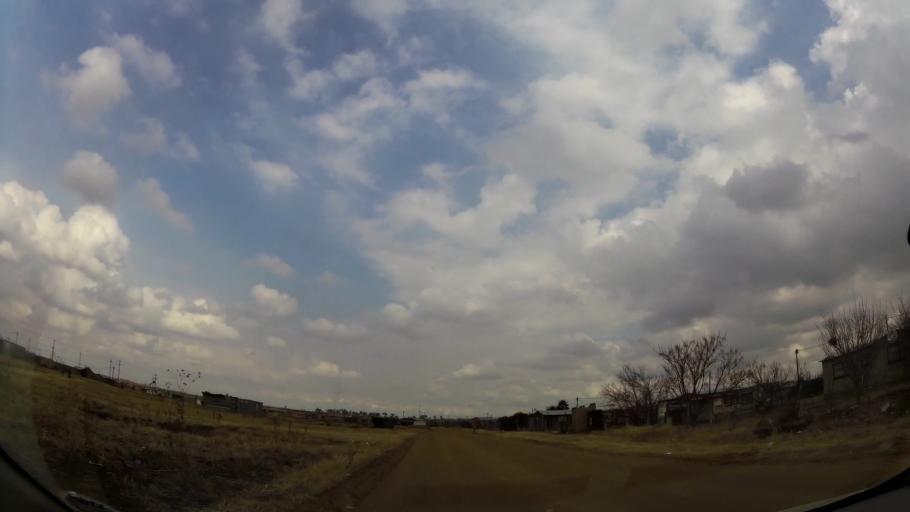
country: ZA
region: Orange Free State
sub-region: Fezile Dabi District Municipality
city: Sasolburg
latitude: -26.8602
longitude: 27.8949
